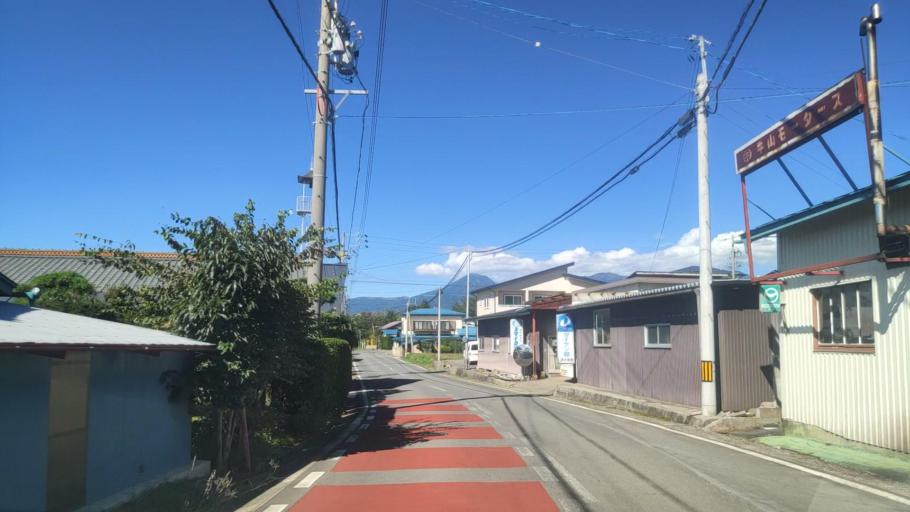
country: JP
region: Nagano
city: Chino
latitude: 35.9789
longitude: 138.2194
